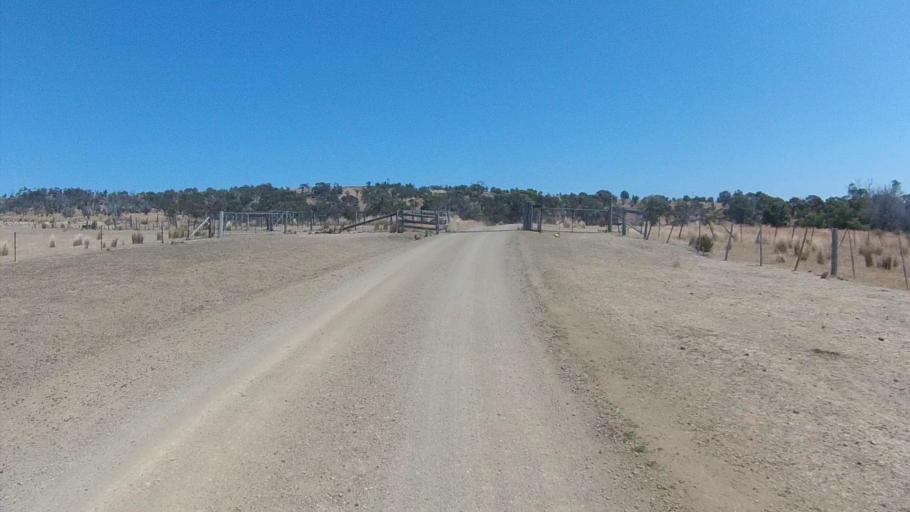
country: AU
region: Tasmania
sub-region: Sorell
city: Sorell
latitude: -42.8958
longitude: 147.8398
